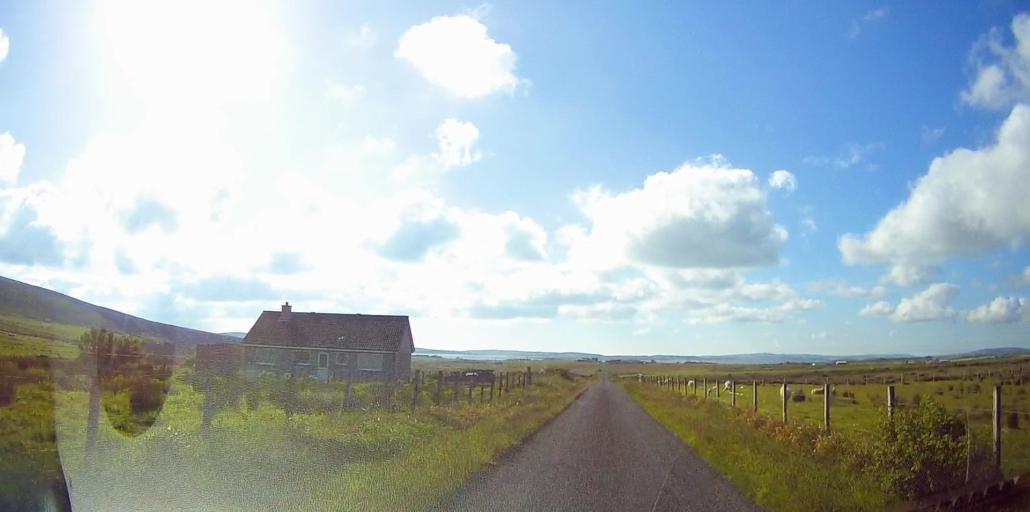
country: GB
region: Scotland
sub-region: Orkney Islands
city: Stromness
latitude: 58.9790
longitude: -3.1746
